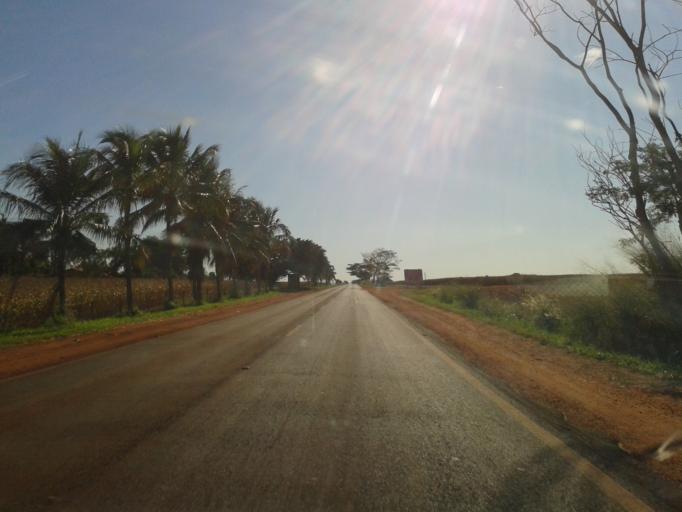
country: BR
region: Minas Gerais
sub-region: Capinopolis
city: Capinopolis
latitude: -18.5975
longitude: -49.5203
